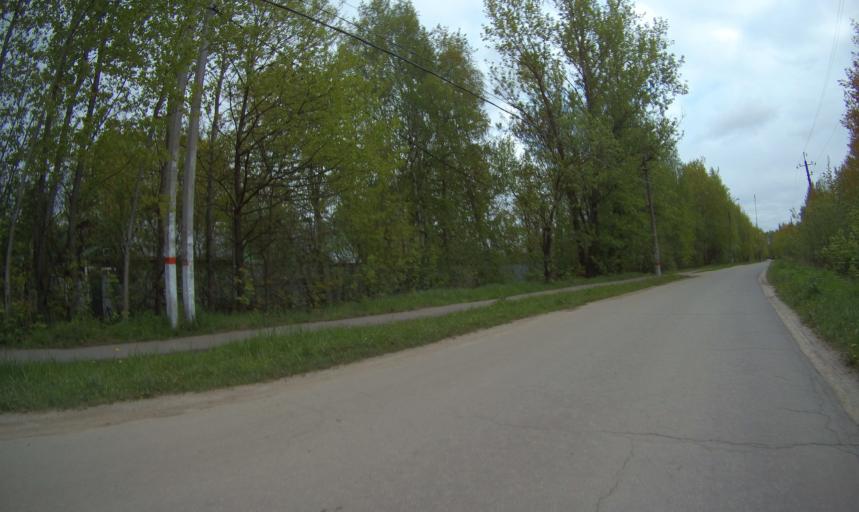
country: RU
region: Moskovskaya
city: Rechitsy
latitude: 55.6070
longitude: 38.5444
